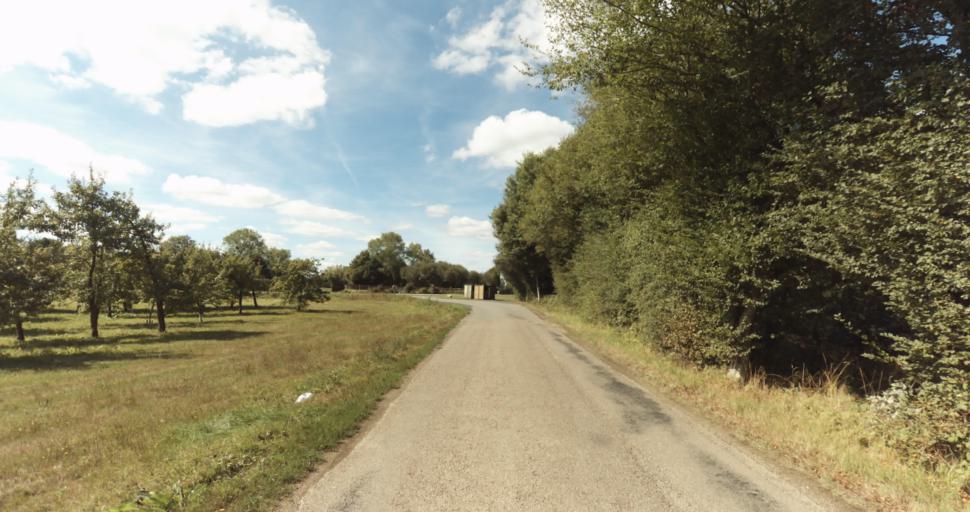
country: FR
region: Lower Normandy
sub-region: Departement de l'Orne
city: Vimoutiers
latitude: 48.9289
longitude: 0.2464
